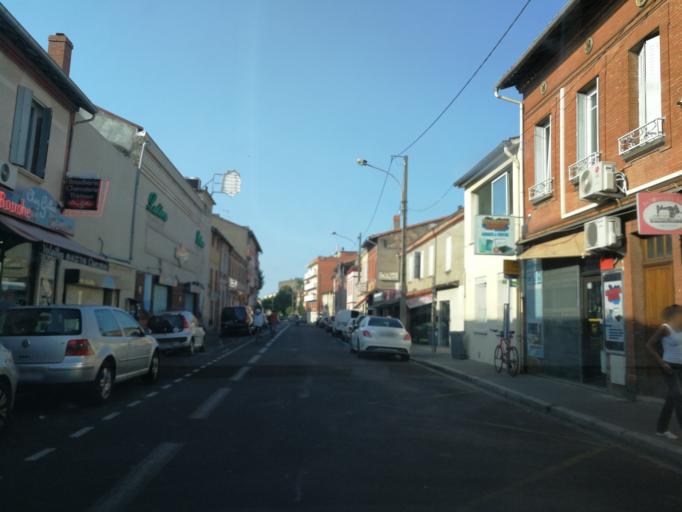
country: FR
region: Midi-Pyrenees
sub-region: Departement de la Haute-Garonne
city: Toulouse
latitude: 43.6186
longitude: 1.4369
